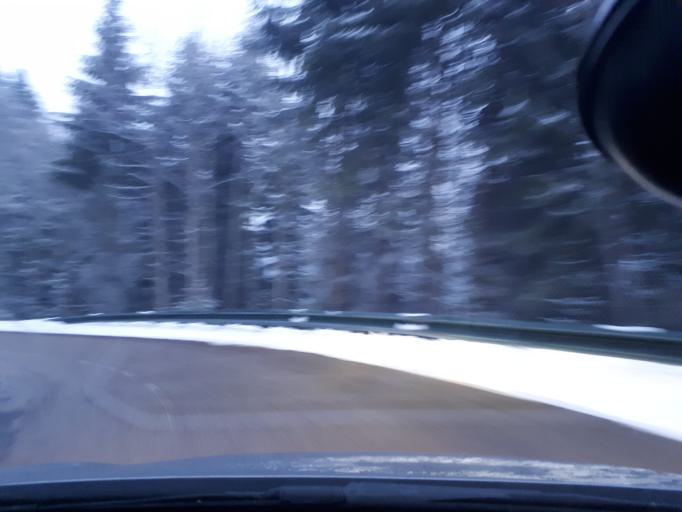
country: FR
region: Rhone-Alpes
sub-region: Departement de l'Isere
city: Vaulnaveys-le-Bas
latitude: 45.1034
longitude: 5.8510
